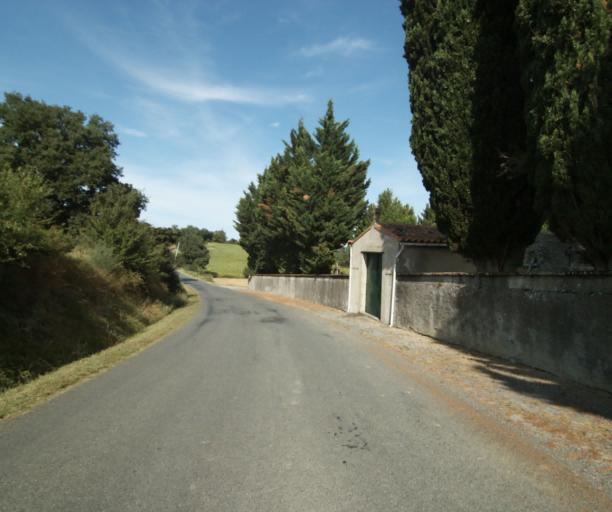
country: FR
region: Midi-Pyrenees
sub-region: Departement du Tarn
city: Puylaurens
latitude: 43.5247
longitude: 2.0555
